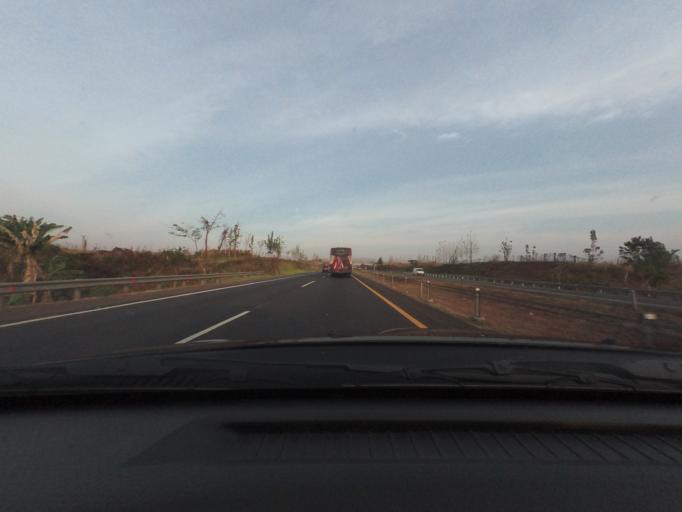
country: ID
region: West Java
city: Pamanukan
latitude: -6.5336
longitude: 107.8292
